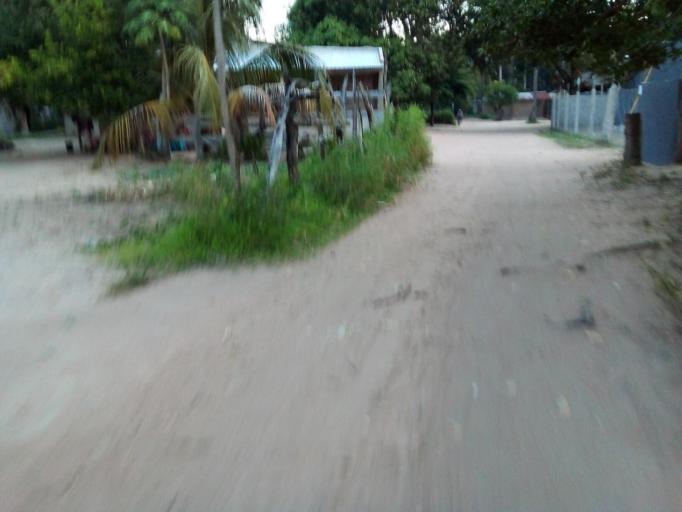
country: MZ
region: Zambezia
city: Quelimane
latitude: -17.6044
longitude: 36.8143
